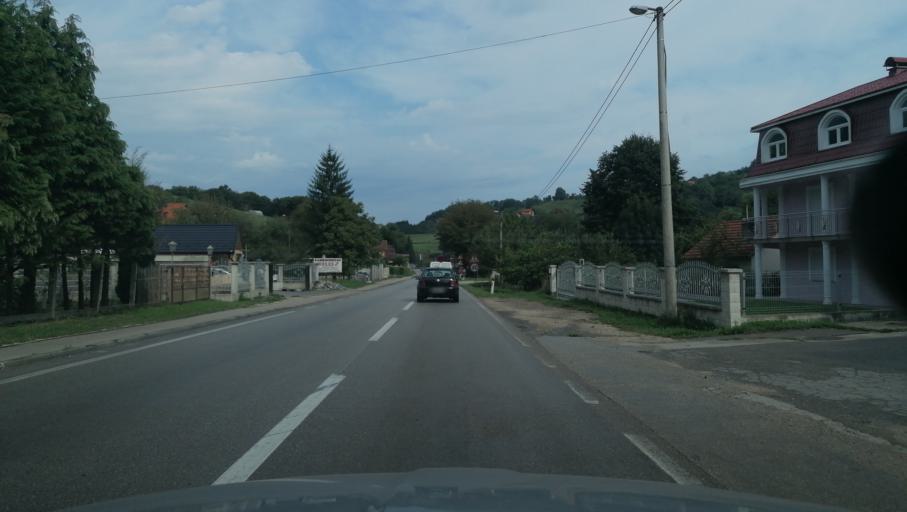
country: BA
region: Republika Srpska
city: Starcevica
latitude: 44.6954
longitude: 17.1969
